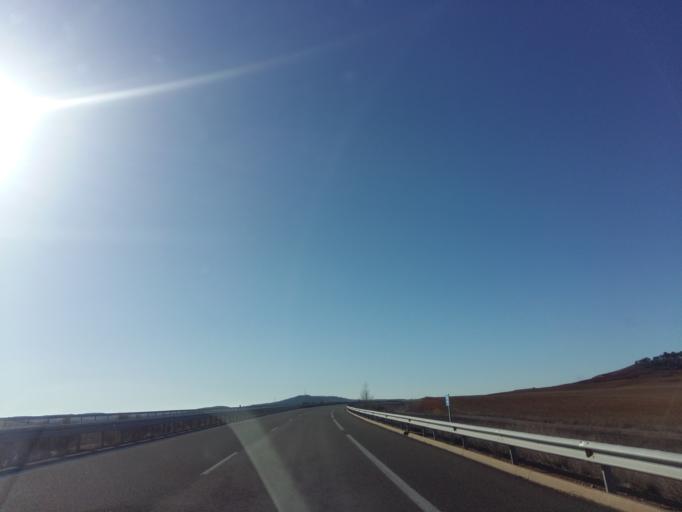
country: ES
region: Castille and Leon
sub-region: Provincia de Palencia
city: Herrera de Pisuerga
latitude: 42.5791
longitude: -4.3461
